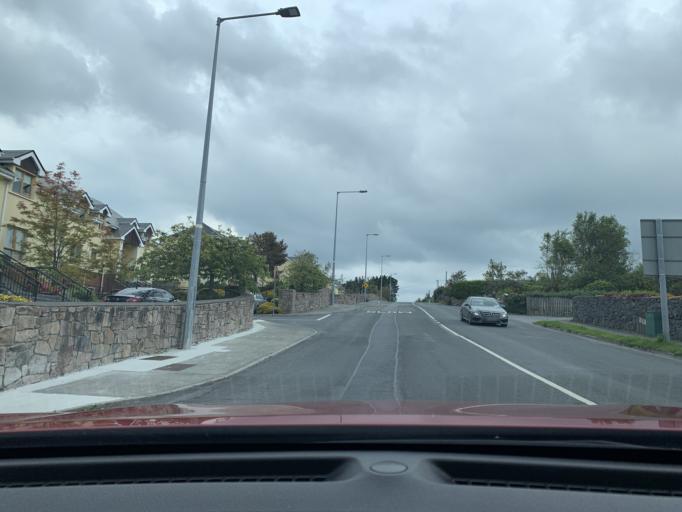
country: IE
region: Connaught
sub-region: County Galway
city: Bearna
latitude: 53.2686
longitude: -9.1176
